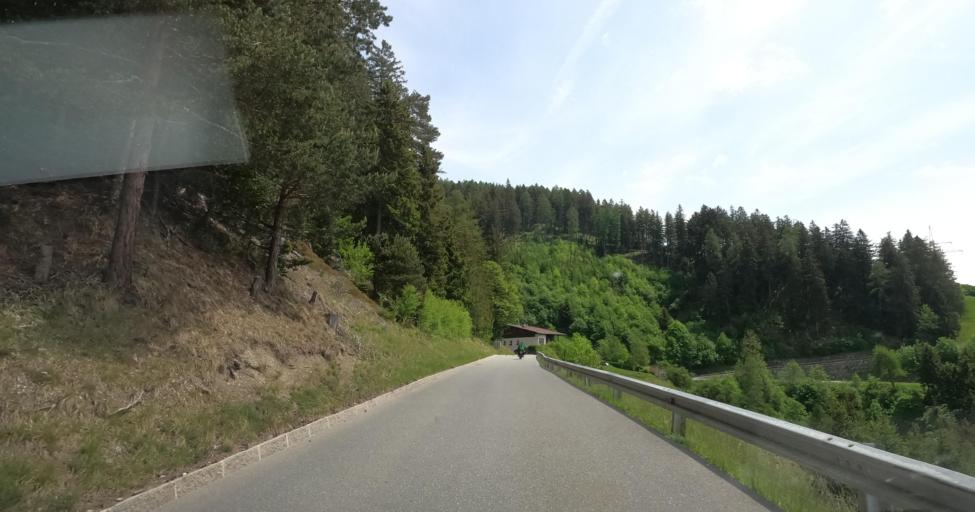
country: AT
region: Tyrol
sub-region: Politischer Bezirk Innsbruck Land
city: Patsch
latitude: 47.1986
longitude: 11.4232
